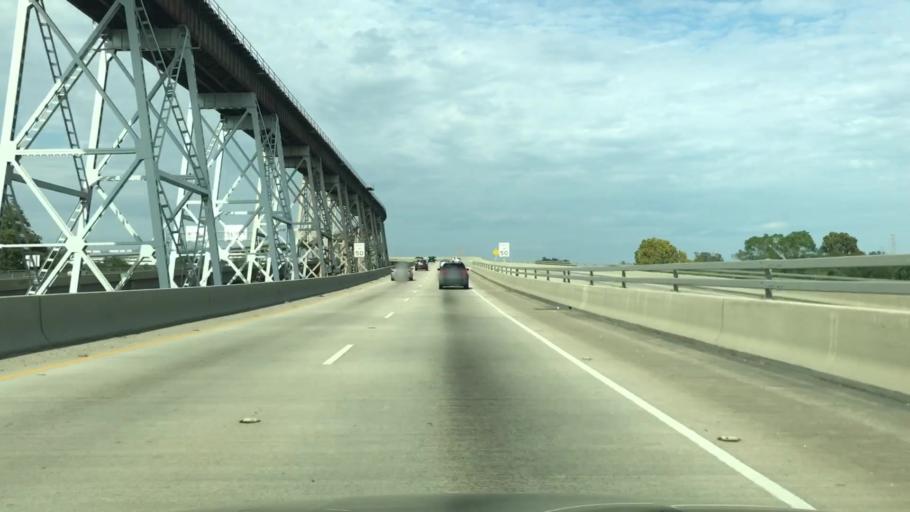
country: US
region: Louisiana
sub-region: Jefferson Parish
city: Bridge City
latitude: 29.9331
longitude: -90.1640
